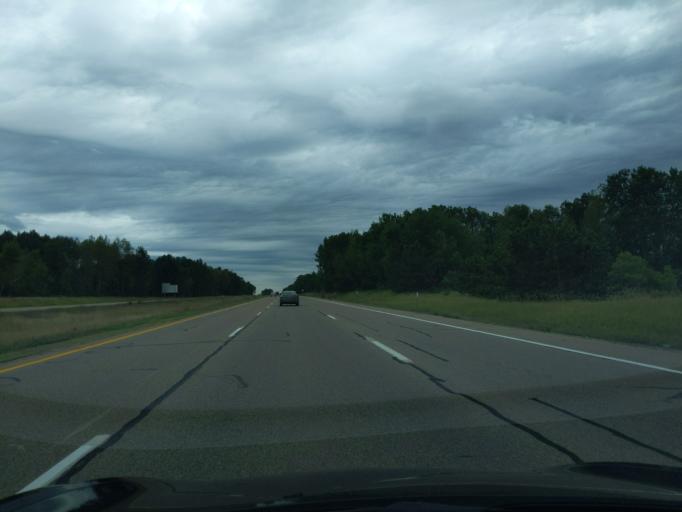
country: US
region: Michigan
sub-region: Roscommon County
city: Houghton Lake
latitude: 44.3320
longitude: -84.8075
